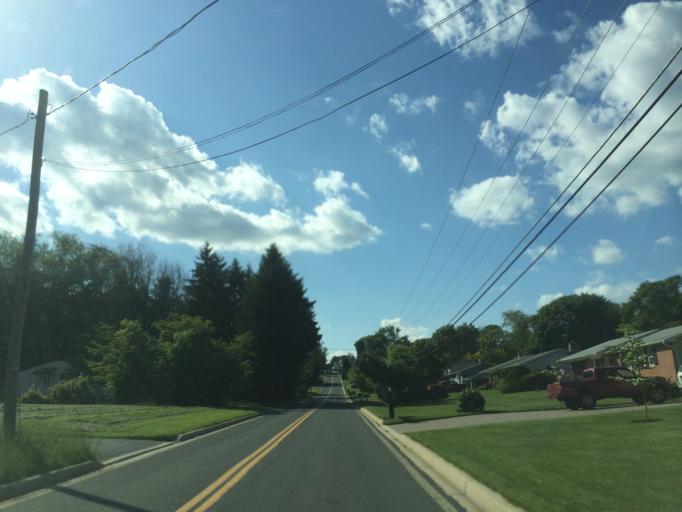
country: US
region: Maryland
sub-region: Carroll County
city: Eldersburg
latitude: 39.4516
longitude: -76.9909
